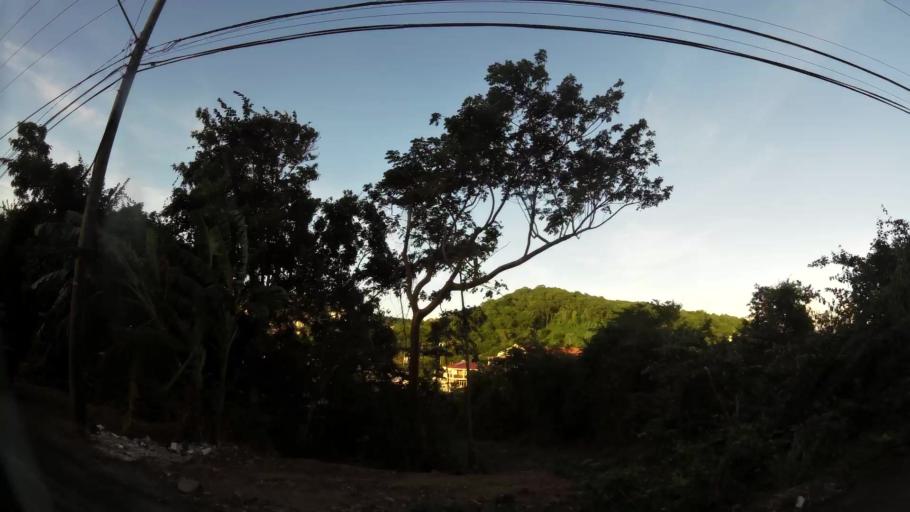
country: LC
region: Gros-Islet
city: Gros Islet
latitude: 14.0769
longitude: -60.9437
